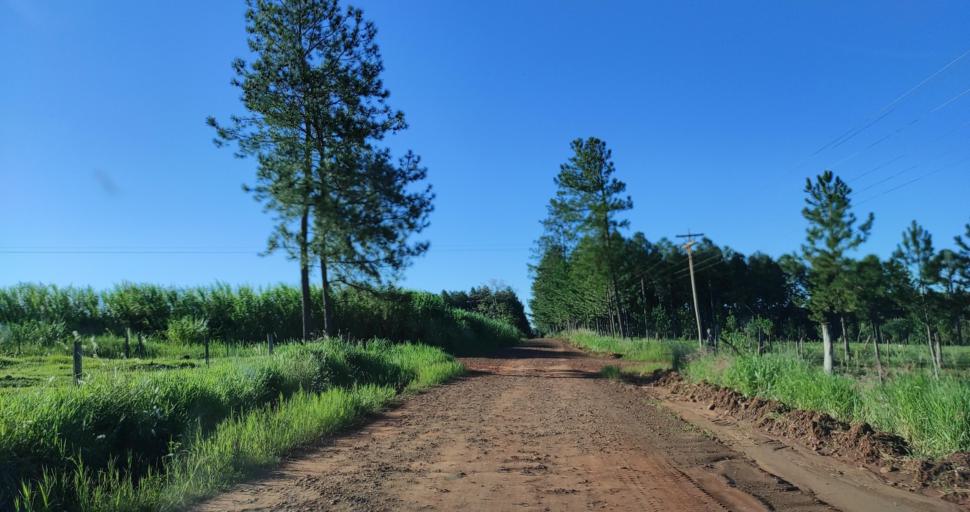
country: AR
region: Misiones
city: Puerto Rico
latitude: -26.8440
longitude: -55.0028
